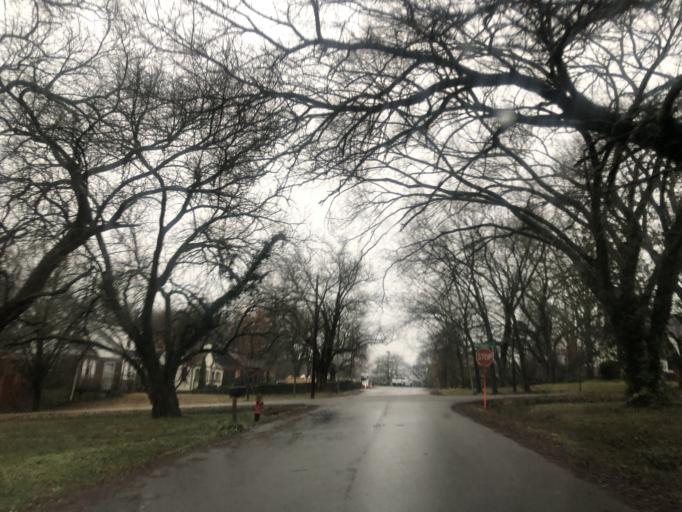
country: US
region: Tennessee
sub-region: Davidson County
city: Oak Hill
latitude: 36.1233
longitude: -86.7987
